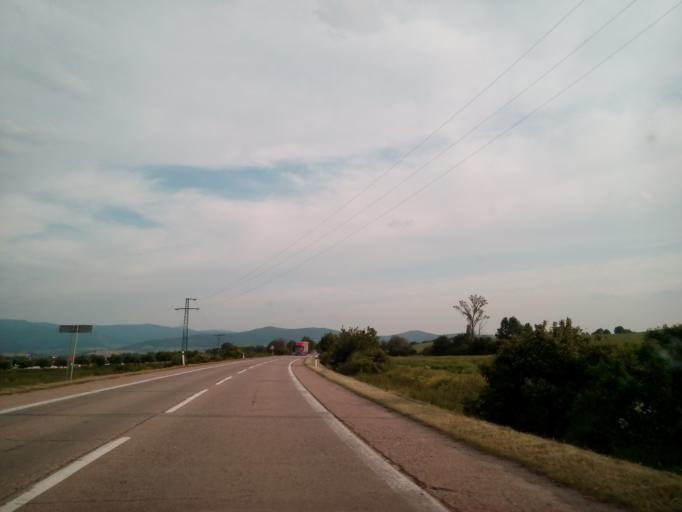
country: SK
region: Trenciansky
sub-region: Okres Trencin
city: Trencin
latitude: 48.8828
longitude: 17.9627
